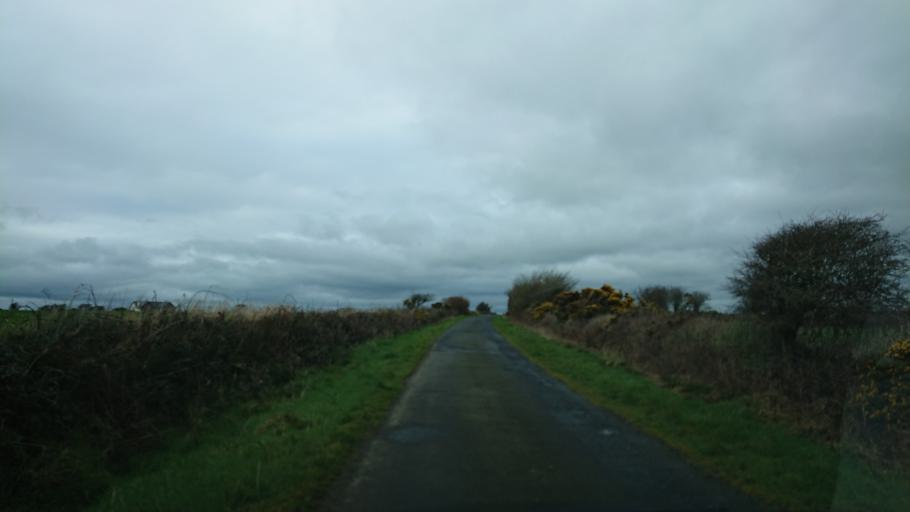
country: IE
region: Munster
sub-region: Waterford
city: Dunmore East
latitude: 52.1499
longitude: -7.0425
